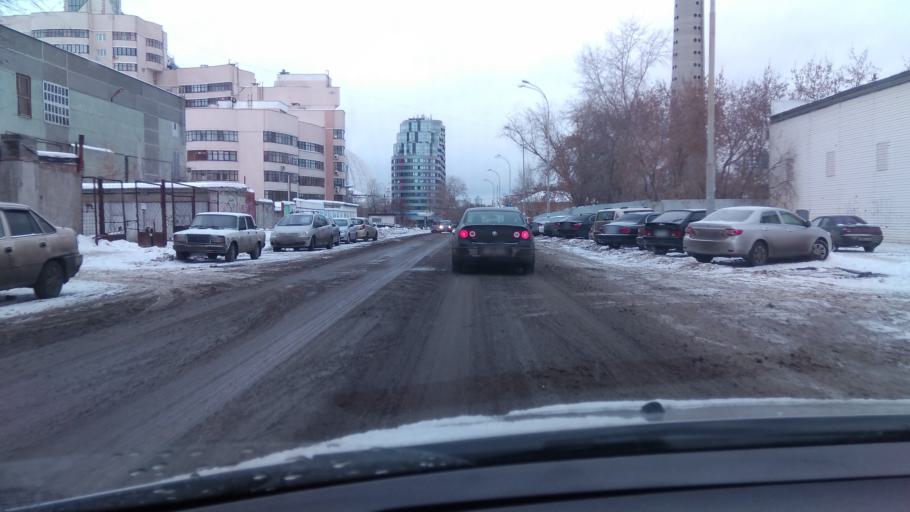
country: RU
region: Sverdlovsk
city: Yekaterinburg
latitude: 56.8211
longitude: 60.6085
